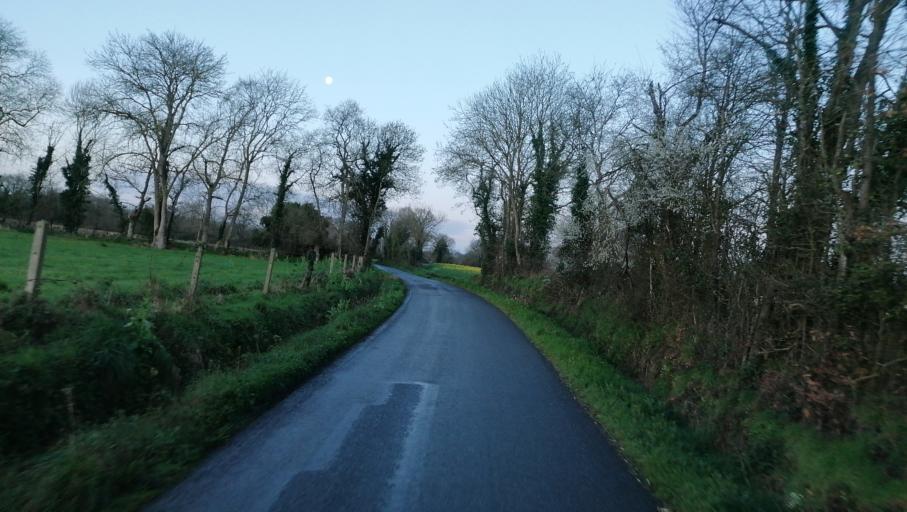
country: FR
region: Brittany
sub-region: Departement des Cotes-d'Armor
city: Plouha
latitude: 48.6680
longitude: -2.9336
